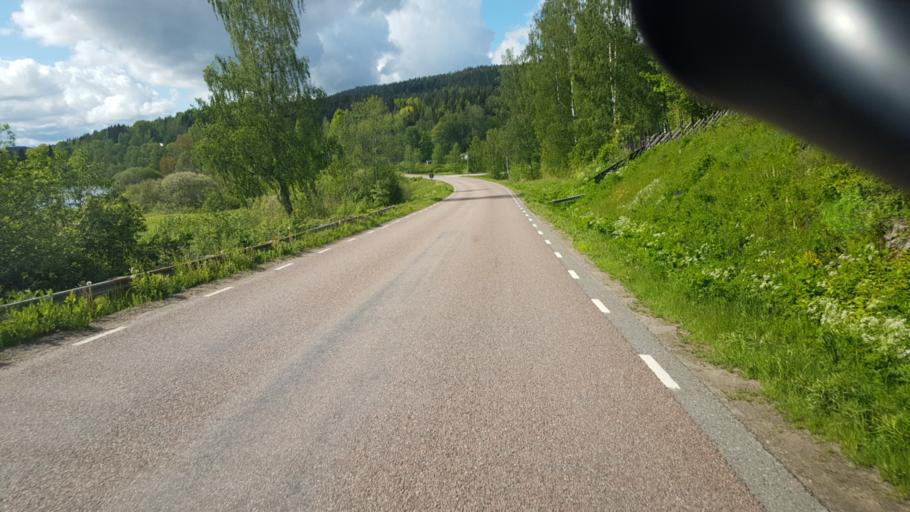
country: NO
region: Ostfold
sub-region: Romskog
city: Romskog
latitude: 59.8105
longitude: 12.0086
